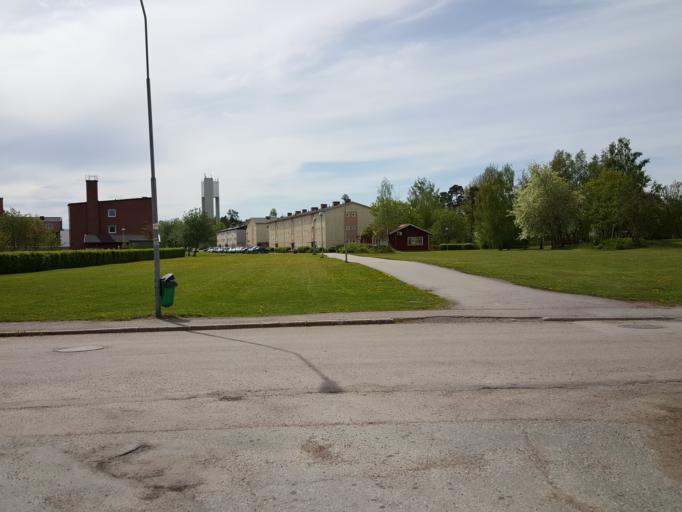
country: SE
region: Uppsala
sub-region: Osthammars Kommun
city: Gimo
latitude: 60.1751
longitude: 18.1832
